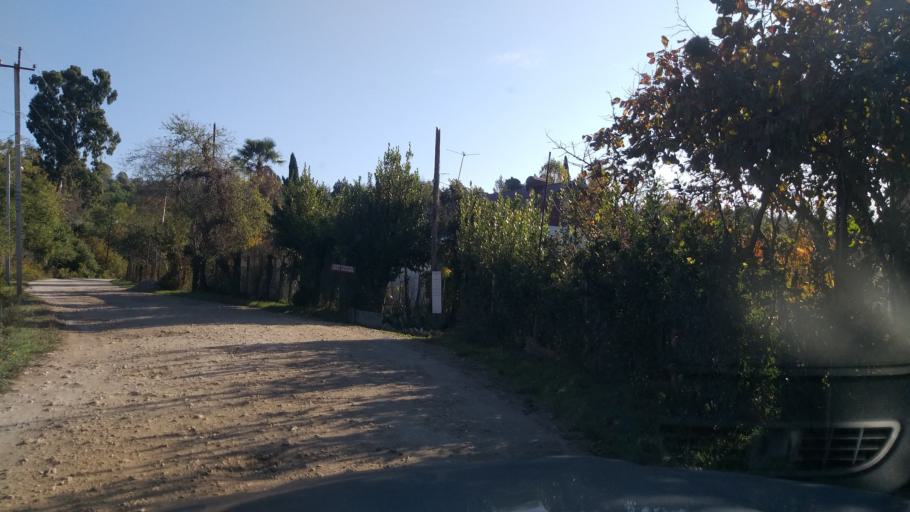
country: GE
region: Abkhazia
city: Stantsiya Novyy Afon
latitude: 43.0654
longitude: 40.8816
